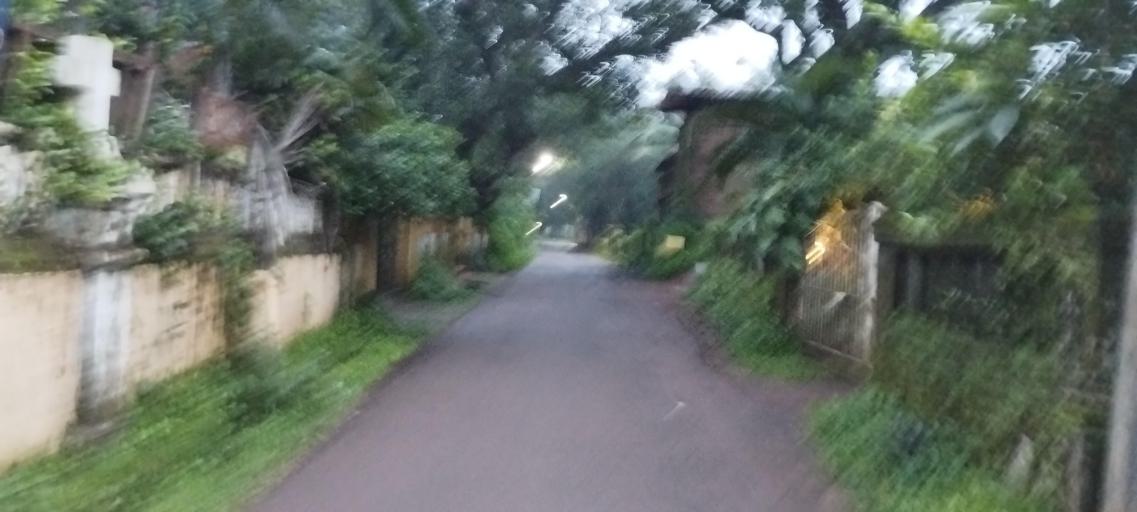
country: IN
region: Goa
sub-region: North Goa
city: Solim
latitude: 15.5990
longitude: 73.7755
